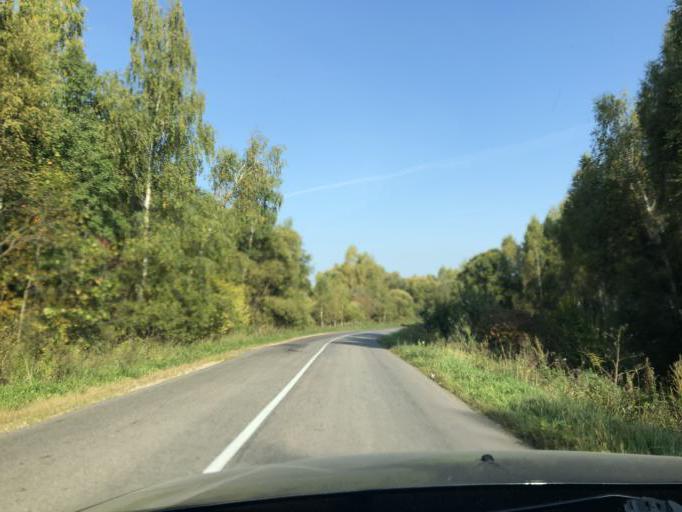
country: RU
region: Tula
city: Novogurovskiy
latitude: 54.3739
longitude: 37.3262
